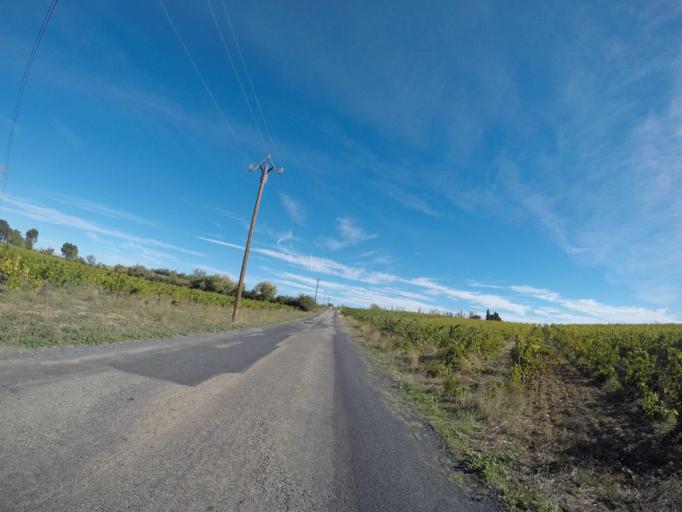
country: FR
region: Languedoc-Roussillon
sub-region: Departement des Pyrenees-Orientales
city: Trouillas
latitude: 42.5943
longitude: 2.8063
